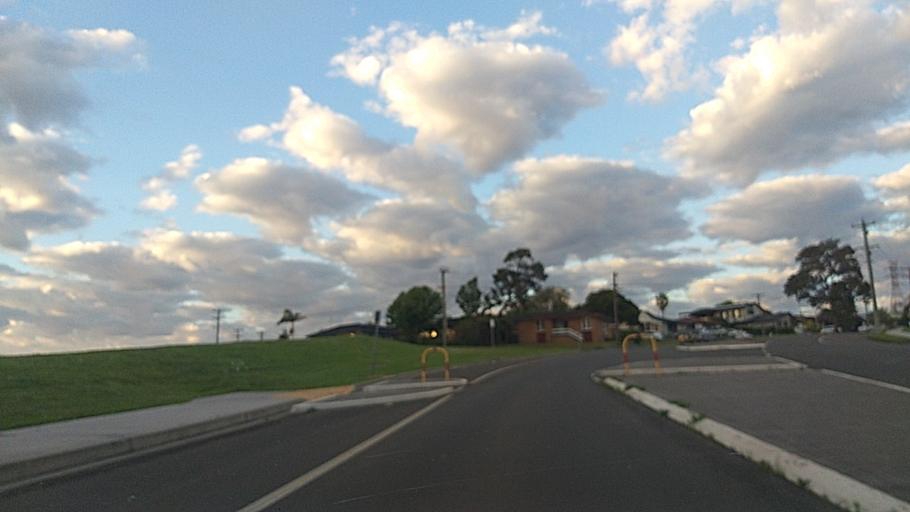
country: AU
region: New South Wales
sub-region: Wollongong
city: Koonawarra
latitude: -34.5025
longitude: 150.8135
